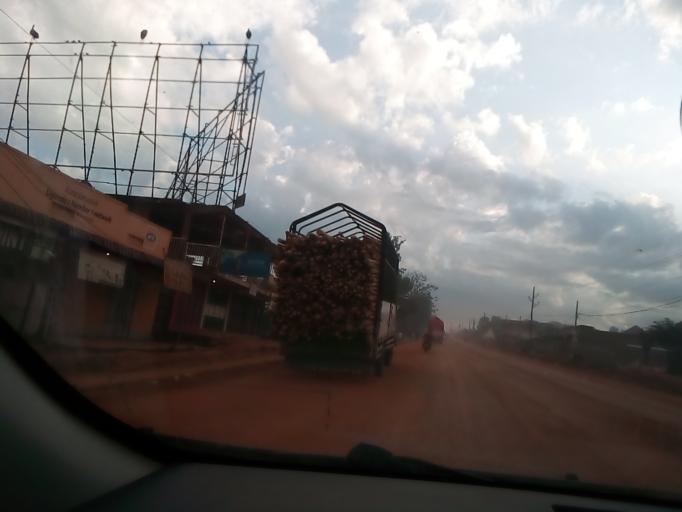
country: UG
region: Central Region
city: Masaka
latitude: -0.3140
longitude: 31.7613
